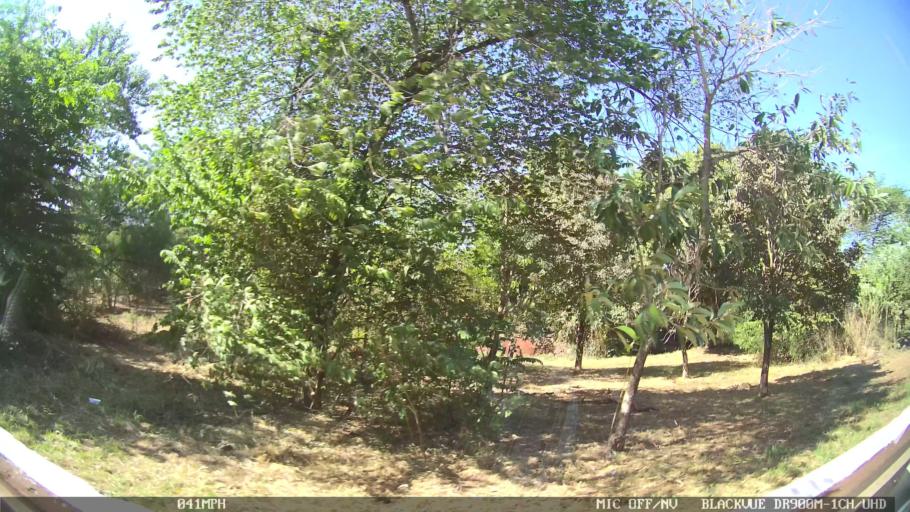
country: BR
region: Sao Paulo
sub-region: Ribeirao Preto
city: Ribeirao Preto
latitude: -21.2366
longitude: -47.7646
